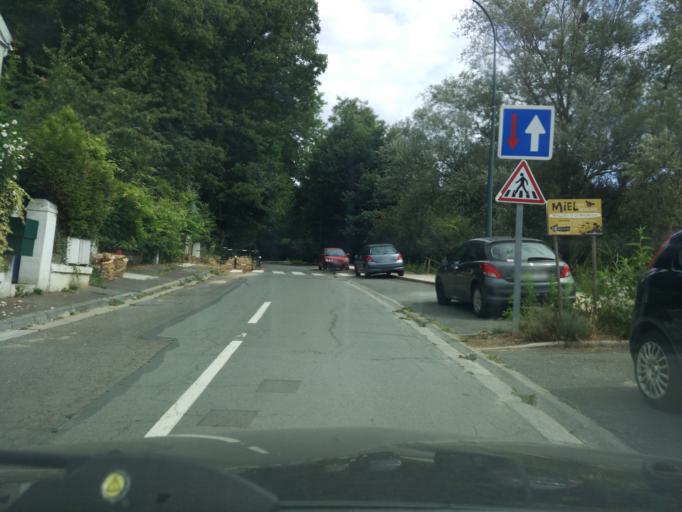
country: FR
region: Ile-de-France
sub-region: Departement de l'Essonne
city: Villiers-le-Bacle
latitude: 48.7191
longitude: 2.1212
